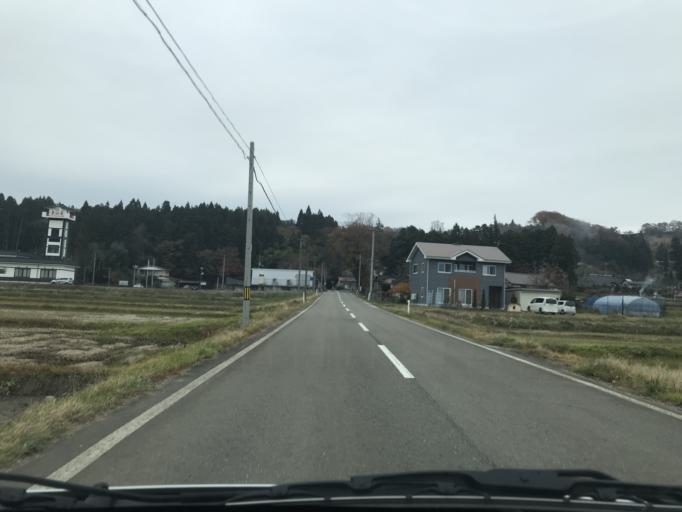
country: JP
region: Iwate
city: Mizusawa
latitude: 39.0328
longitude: 141.0755
